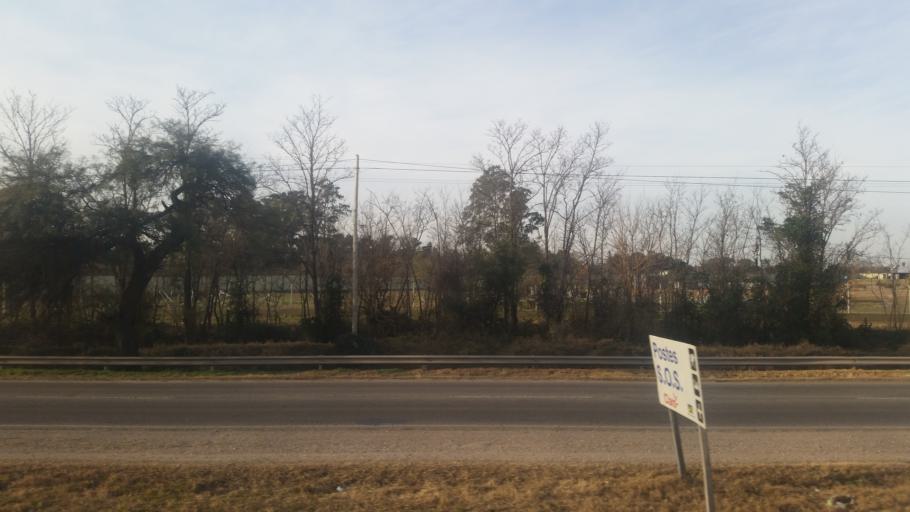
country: AR
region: Cordoba
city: Malvinas Argentinas
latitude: -31.4728
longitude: -64.0952
